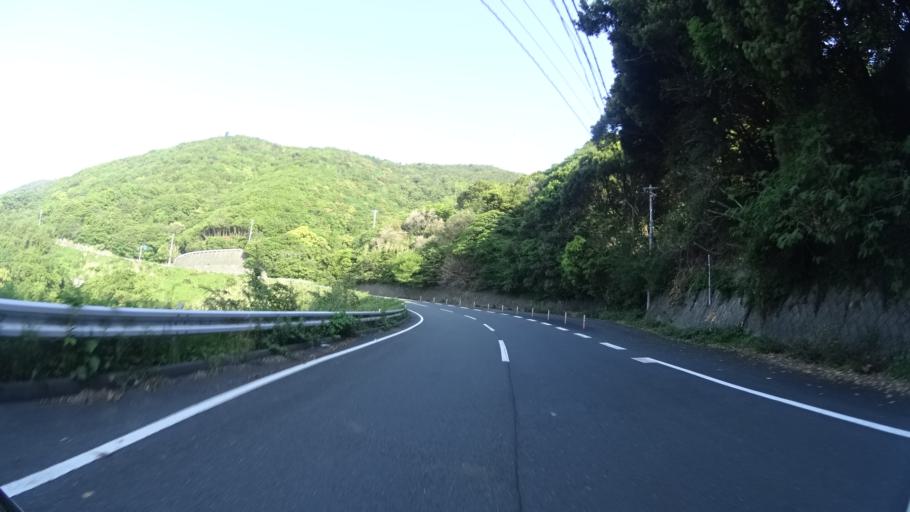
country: JP
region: Ehime
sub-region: Nishiuwa-gun
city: Ikata-cho
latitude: 33.3894
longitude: 132.0951
